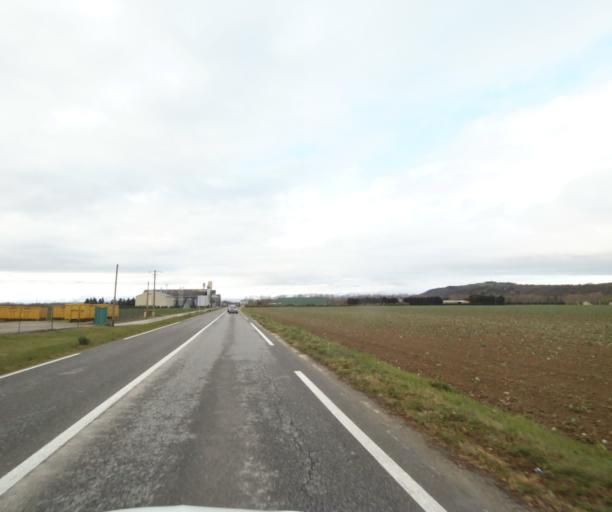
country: FR
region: Midi-Pyrenees
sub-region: Departement de l'Ariege
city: Saverdun
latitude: 43.2029
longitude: 1.6092
